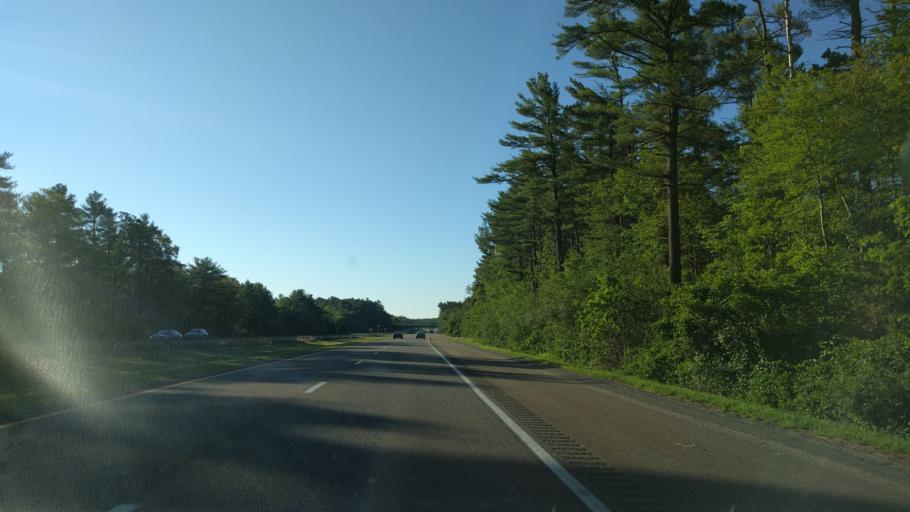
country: US
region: Massachusetts
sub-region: Plymouth County
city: Middleborough Center
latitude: 41.9067
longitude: -70.9713
